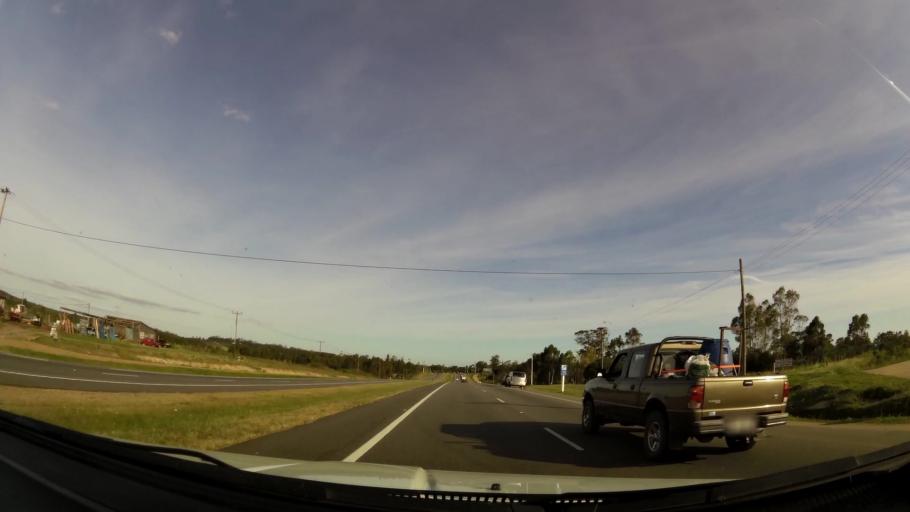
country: UY
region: Canelones
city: La Floresta
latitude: -34.7711
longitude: -55.5744
